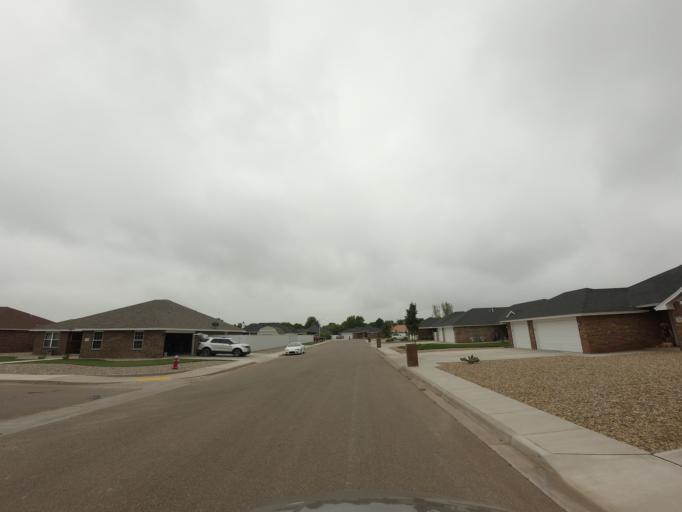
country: US
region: New Mexico
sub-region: Curry County
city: Clovis
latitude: 34.4317
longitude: -103.1816
